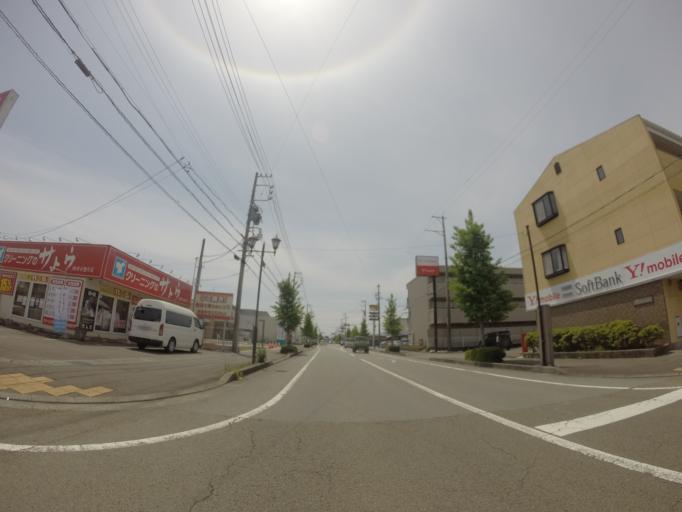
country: JP
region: Shizuoka
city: Yaizu
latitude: 34.8466
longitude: 138.3082
